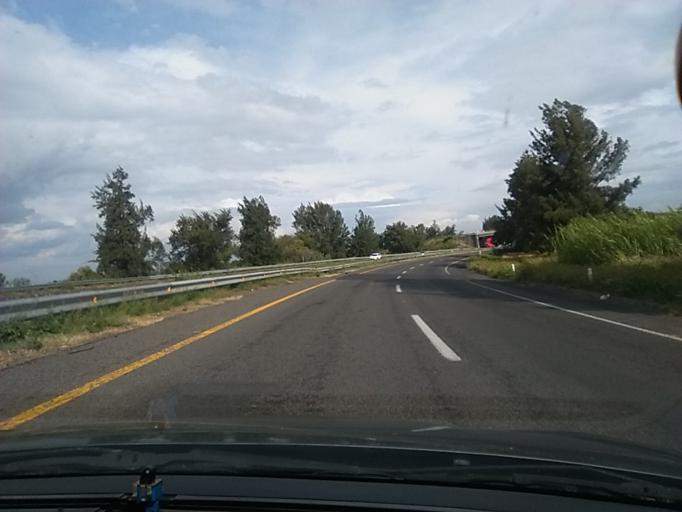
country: MX
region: Jalisco
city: La Barca
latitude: 20.3218
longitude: -102.5076
